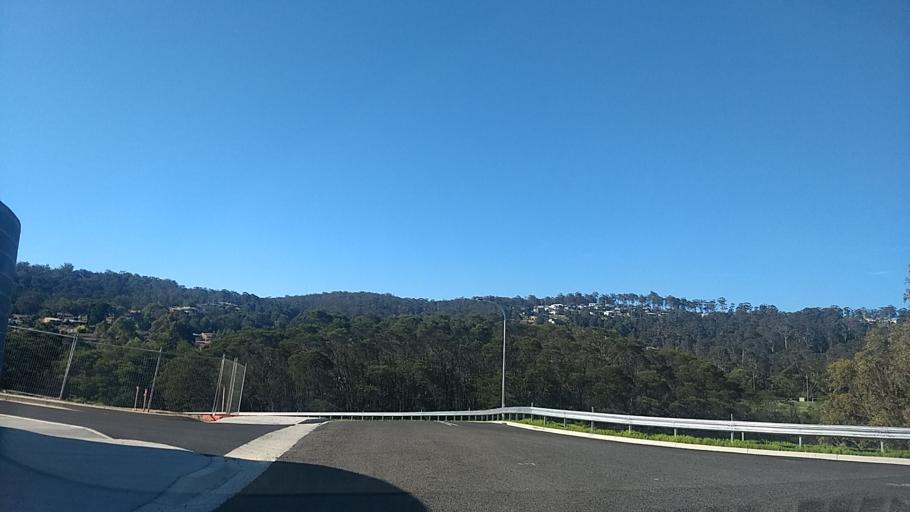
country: AU
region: New South Wales
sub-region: Bega Valley
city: Merimbula
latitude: -36.8858
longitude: 149.9089
